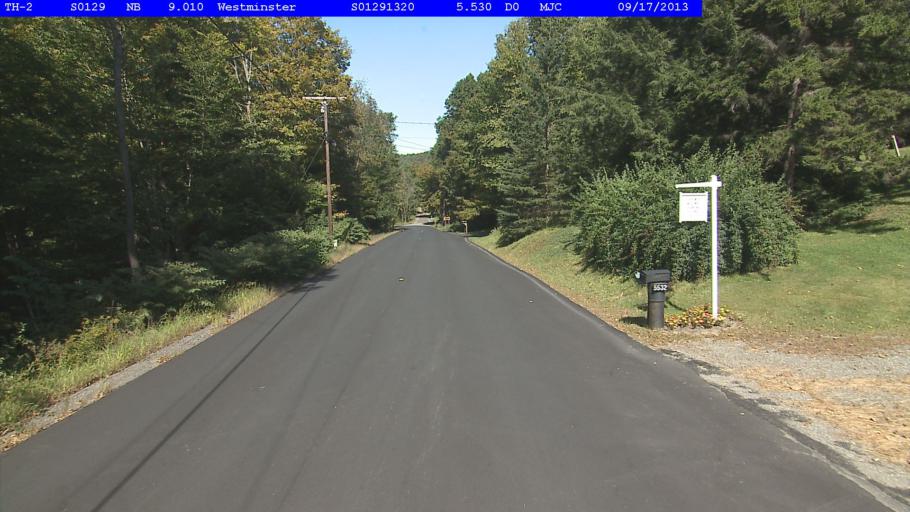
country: US
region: Vermont
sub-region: Windham County
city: Bellows Falls
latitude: 43.0947
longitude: -72.5351
